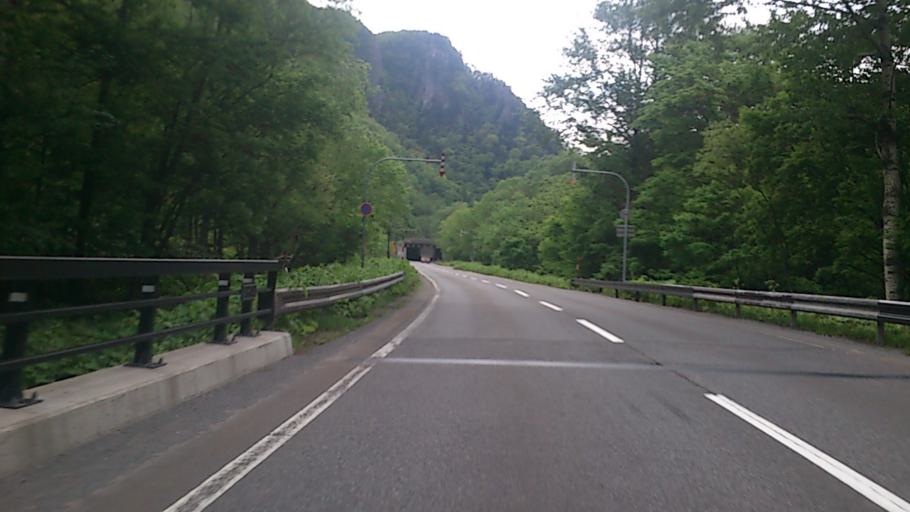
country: JP
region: Hokkaido
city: Kamikawa
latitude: 43.7503
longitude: 142.9320
